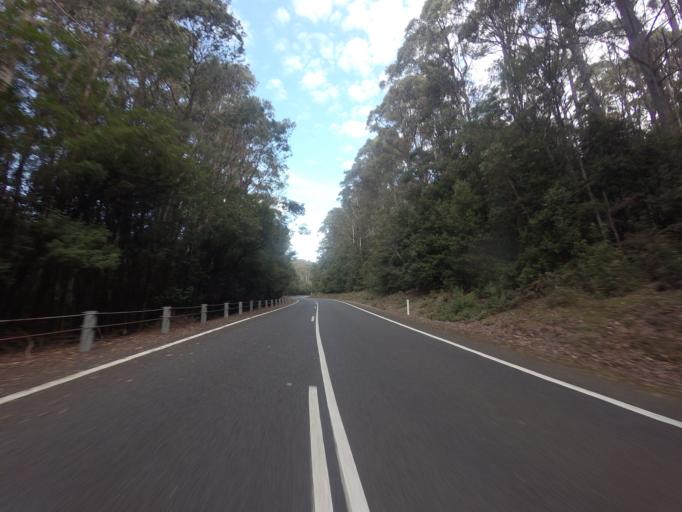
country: AU
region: Tasmania
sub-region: Meander Valley
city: Deloraine
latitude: -41.6436
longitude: 146.7183
